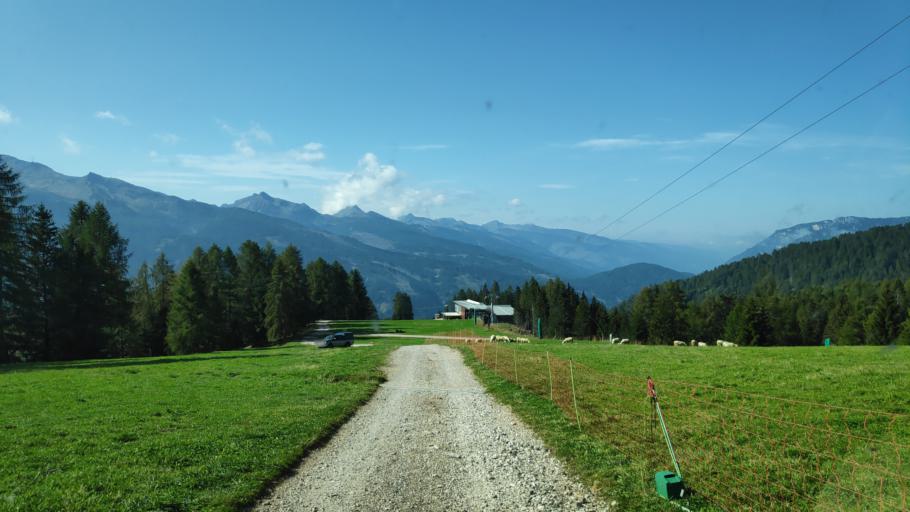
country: IT
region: Trentino-Alto Adige
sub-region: Provincia di Trento
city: Moena
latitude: 46.3264
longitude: 11.7020
